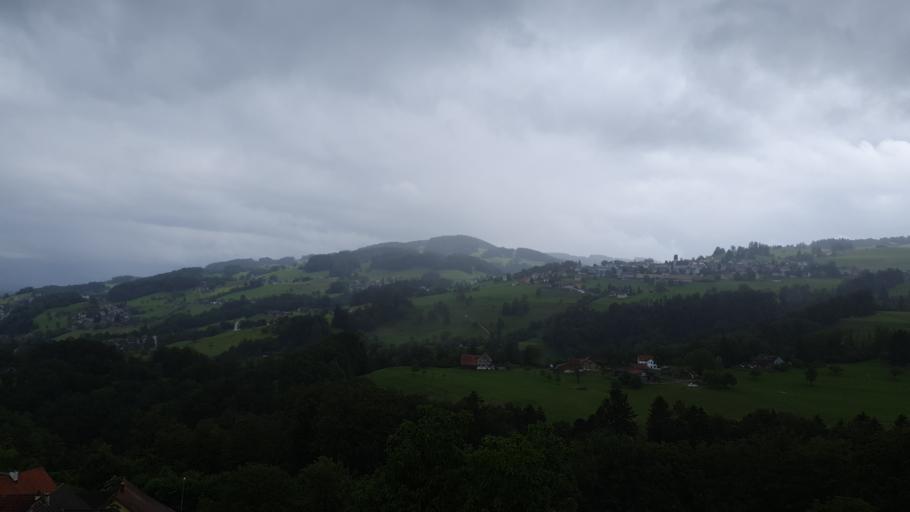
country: CH
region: Appenzell Ausserrhoden
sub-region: Bezirk Vorderland
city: Heiden
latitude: 47.4650
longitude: 9.5400
